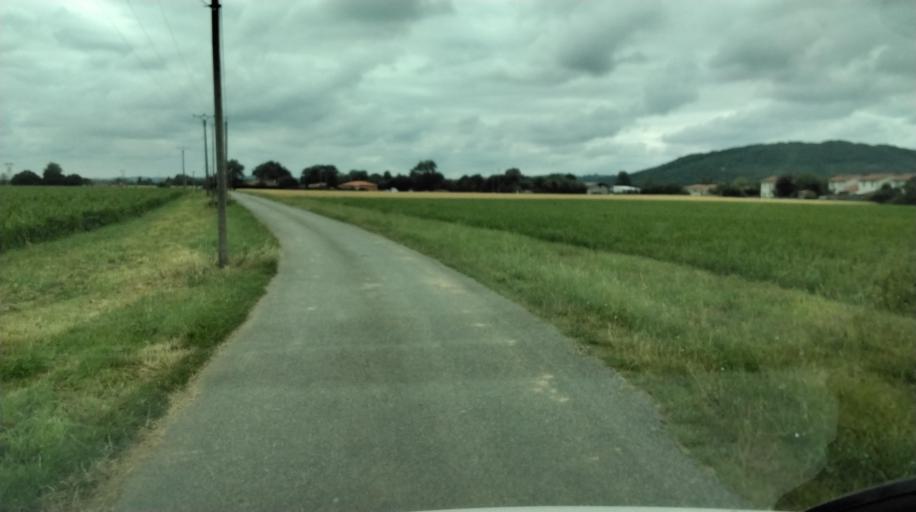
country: FR
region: Midi-Pyrenees
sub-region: Departement de la Haute-Garonne
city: Martres-Tolosane
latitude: 43.2028
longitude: 1.0240
